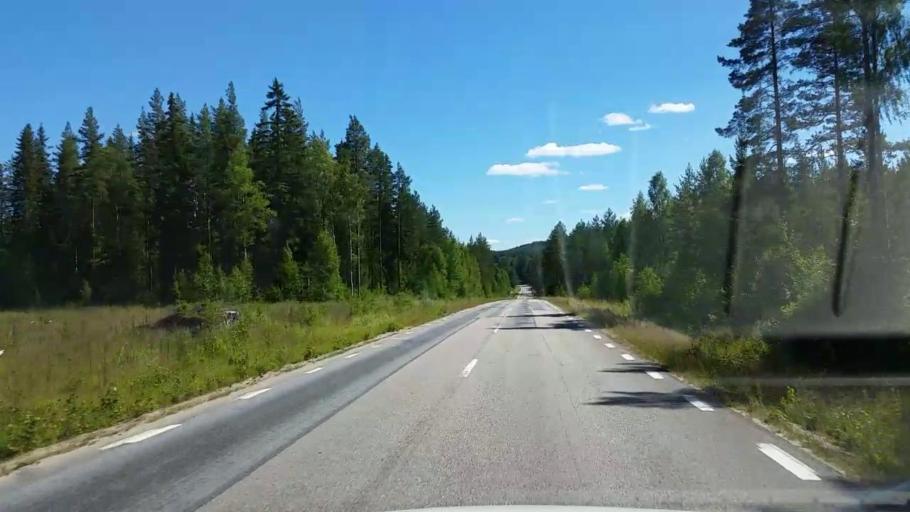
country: SE
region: Gaevleborg
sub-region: Ovanakers Kommun
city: Edsbyn
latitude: 61.3365
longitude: 15.8272
